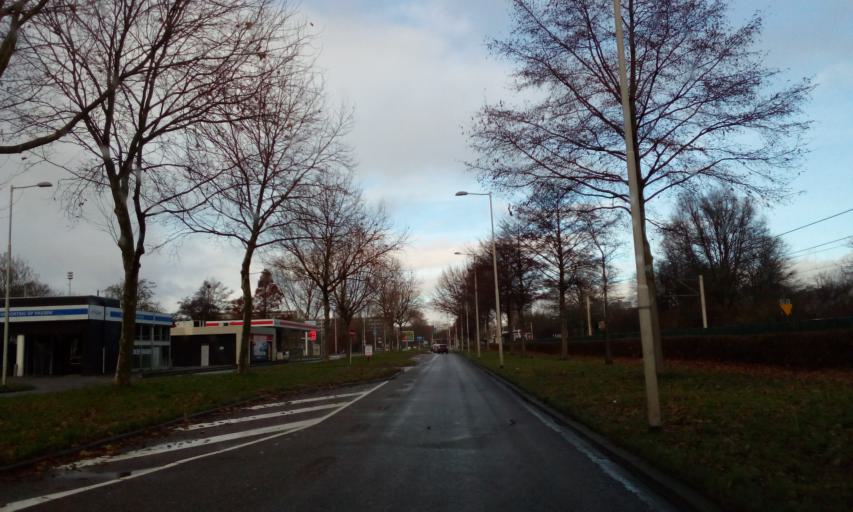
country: NL
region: South Holland
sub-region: Gemeente Rotterdam
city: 's-Gravenland
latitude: 51.9551
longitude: 4.5501
